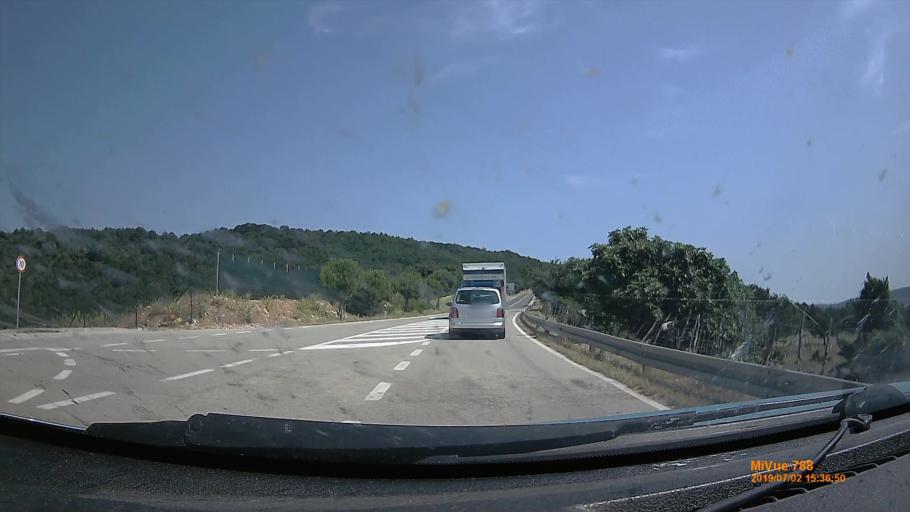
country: HR
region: Primorsko-Goranska
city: Cres
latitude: 44.9821
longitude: 14.4130
